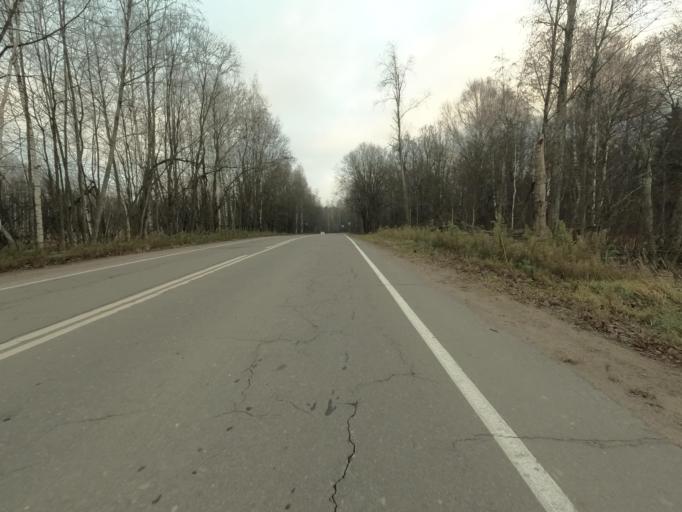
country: RU
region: Leningrad
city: Mga
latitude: 59.7939
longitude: 31.0083
